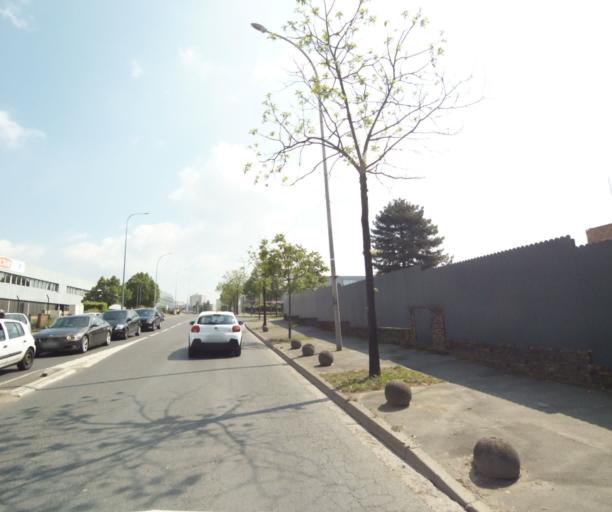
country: FR
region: Ile-de-France
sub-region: Departement des Yvelines
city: Sartrouville
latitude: 48.9512
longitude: 2.2103
